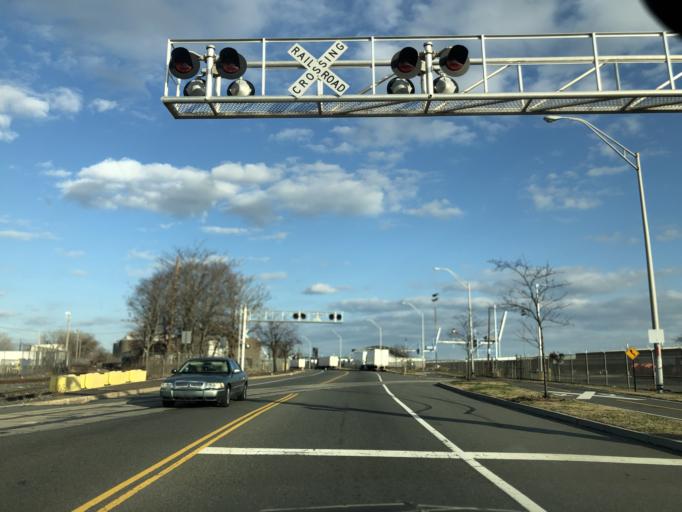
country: US
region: New Jersey
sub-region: Camden County
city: Merchantville
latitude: 39.9794
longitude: -75.0932
